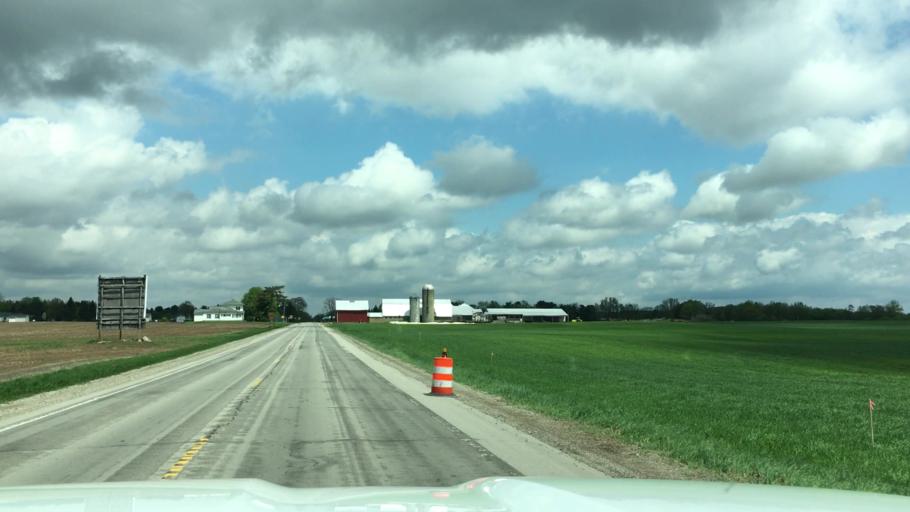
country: US
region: Michigan
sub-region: Ingham County
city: Stockbridge
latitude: 42.4629
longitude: -84.1901
